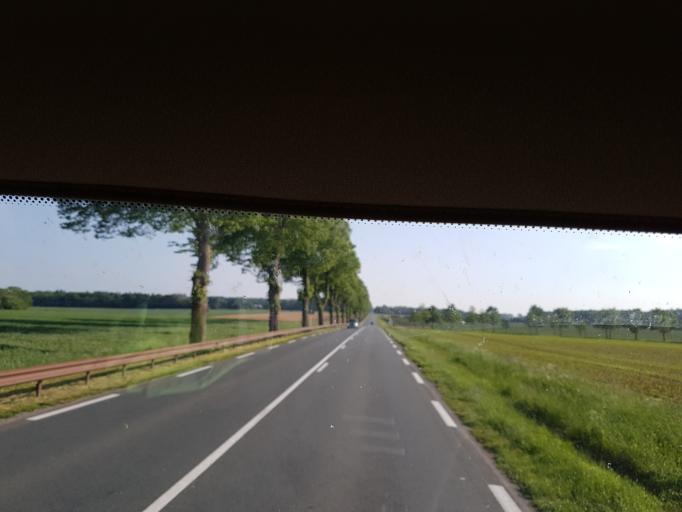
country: FR
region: Picardie
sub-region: Departement de la Somme
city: Abbeville
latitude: 50.1664
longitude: 1.8629
